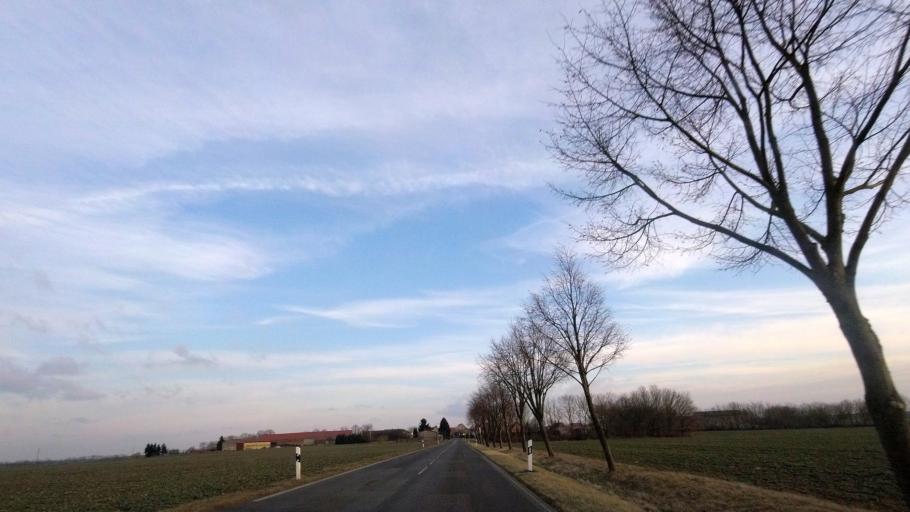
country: DE
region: Brandenburg
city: Belzig
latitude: 52.1047
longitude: 12.5492
